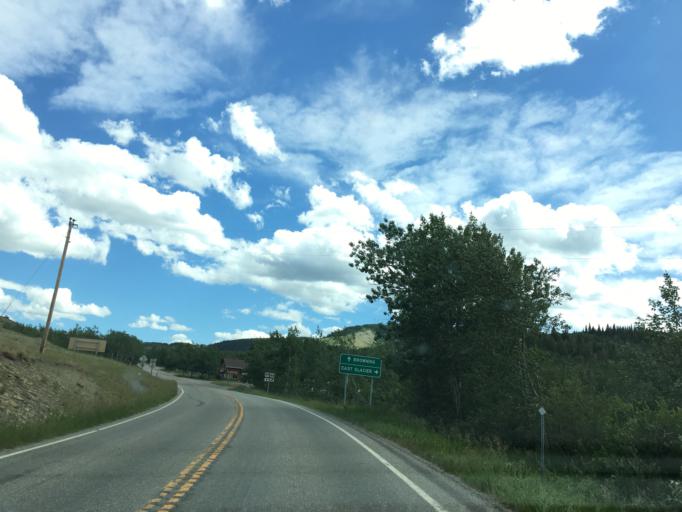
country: US
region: Montana
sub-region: Glacier County
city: South Browning
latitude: 48.5489
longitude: -113.2715
